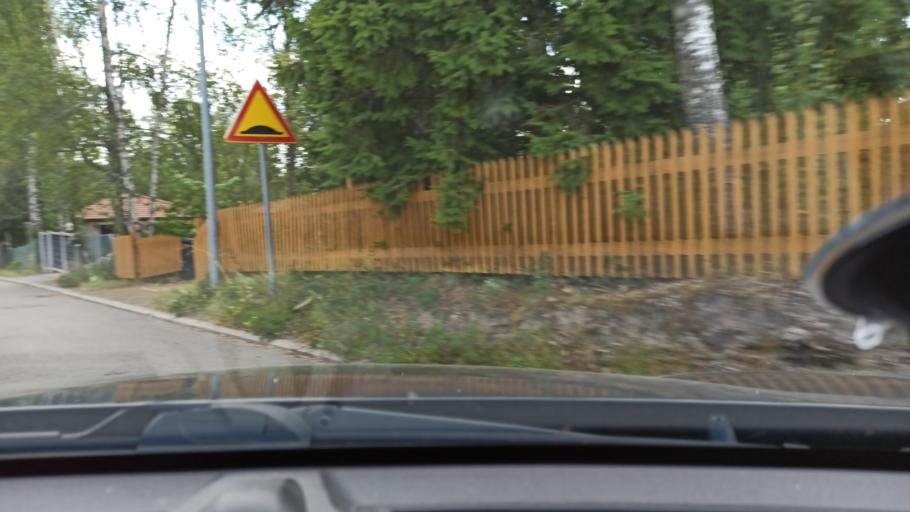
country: FI
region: Uusimaa
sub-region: Helsinki
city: Kirkkonummi
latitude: 60.2751
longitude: 24.4131
